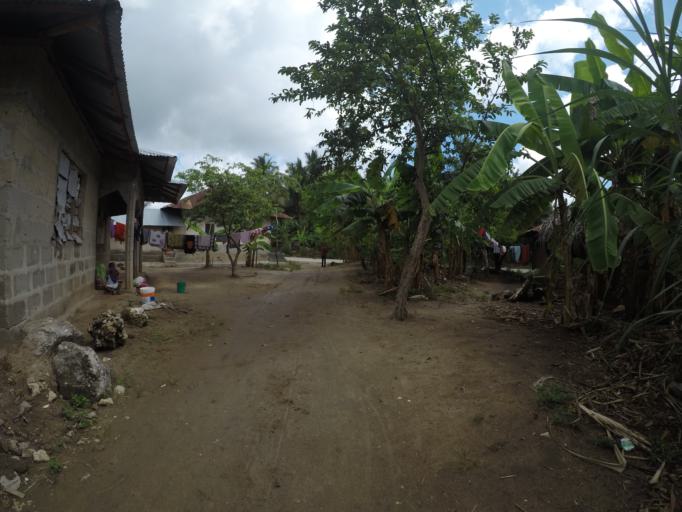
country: TZ
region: Pemba South
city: Mtambile
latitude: -5.3882
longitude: 39.7465
